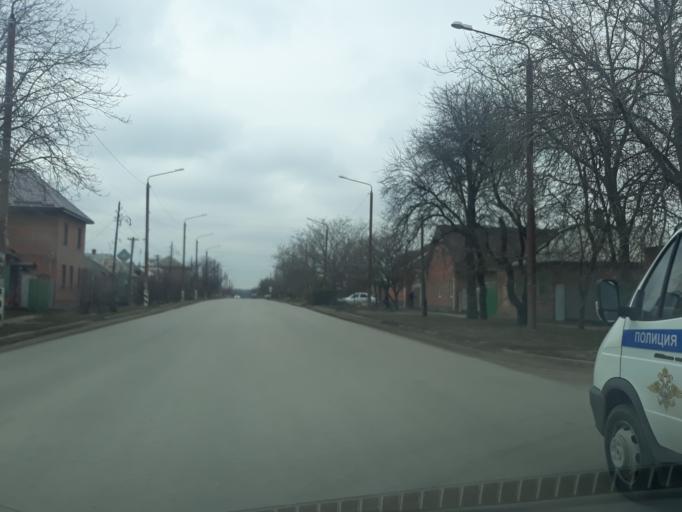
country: RU
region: Rostov
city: Taganrog
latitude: 47.2703
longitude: 38.9003
